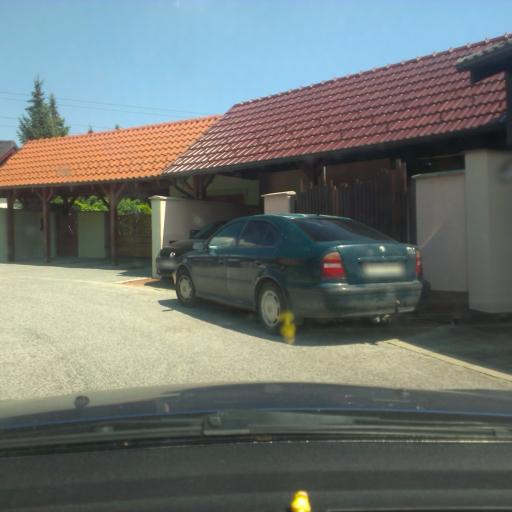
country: SK
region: Trnavsky
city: Hlohovec
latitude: 48.4426
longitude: 17.8144
